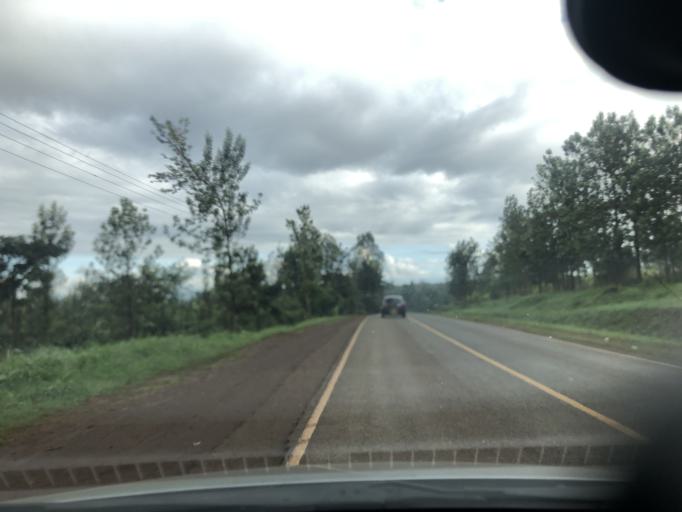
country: KE
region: Murang'a District
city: Maragua
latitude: -0.8265
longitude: 37.1382
